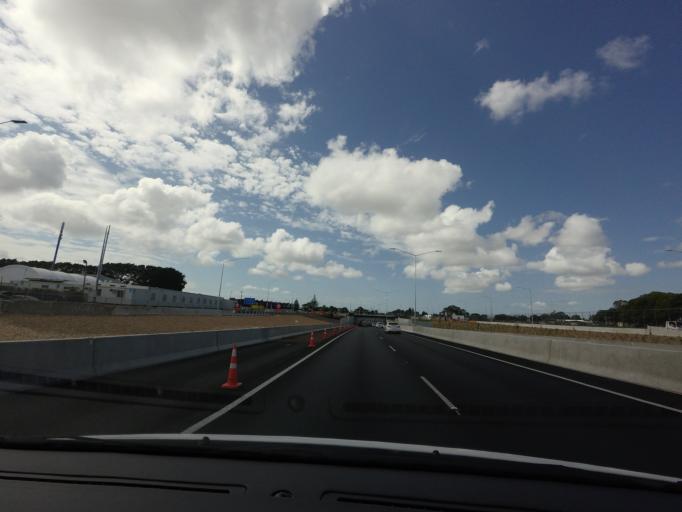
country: NZ
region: Auckland
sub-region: Auckland
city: Mangere
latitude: -36.9754
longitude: 174.7879
